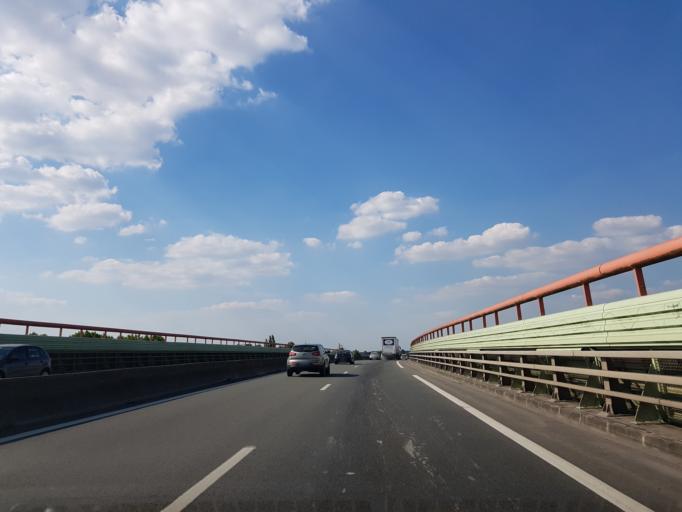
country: FR
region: Nord-Pas-de-Calais
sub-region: Departement du Nord
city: Somain
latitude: 50.3543
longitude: 3.2625
